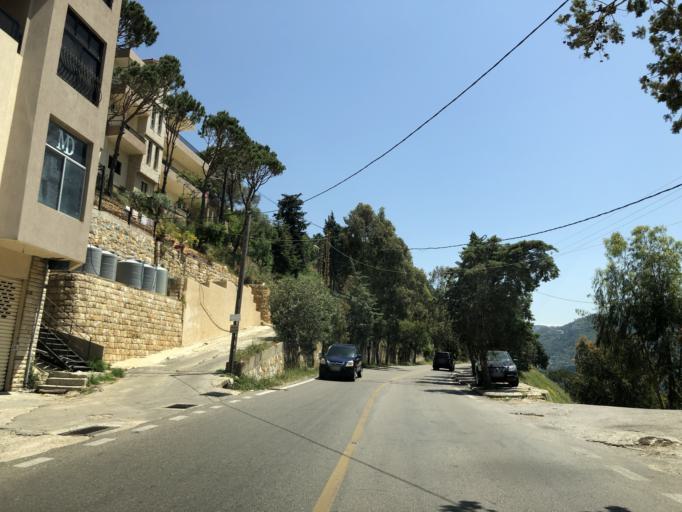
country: LB
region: Mont-Liban
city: Beit ed Dine
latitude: 33.6876
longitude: 35.5220
